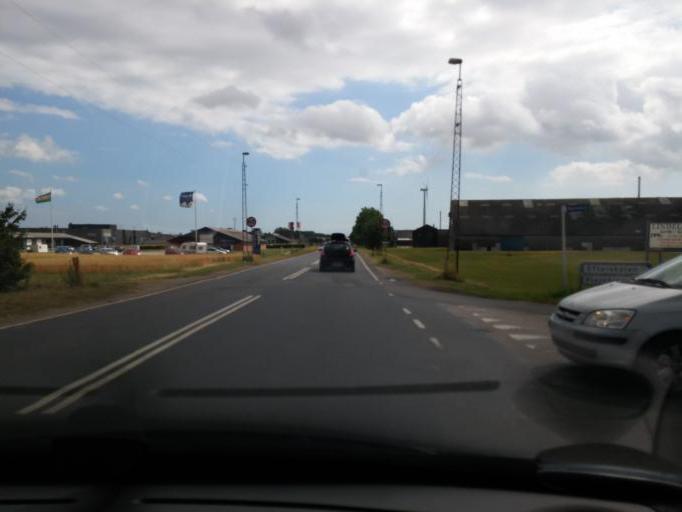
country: DK
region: South Denmark
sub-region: Langeland Kommune
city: Rudkobing
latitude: 54.9424
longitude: 10.7345
